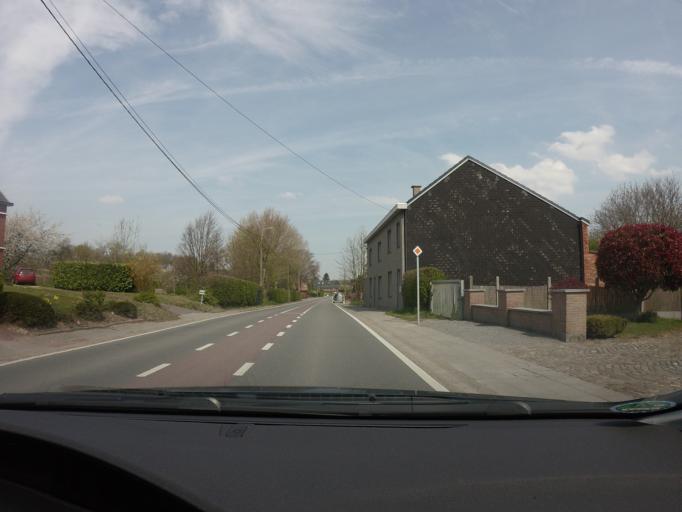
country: NL
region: Limburg
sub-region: Eijsden-Margraten
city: Eijsden
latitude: 50.8007
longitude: 5.6719
